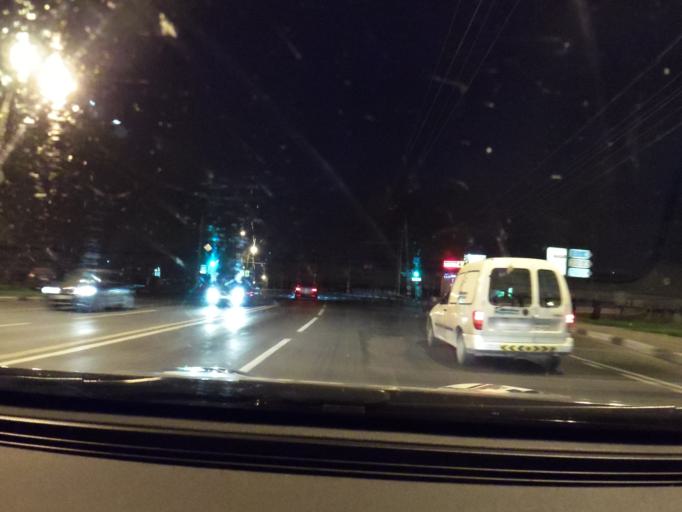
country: RU
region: Nizjnij Novgorod
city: Bor
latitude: 56.3196
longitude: 44.0563
